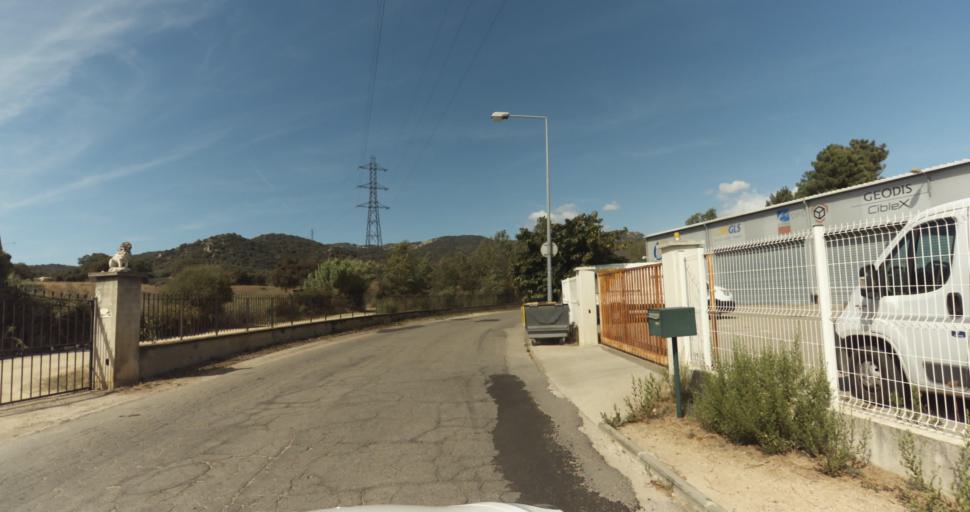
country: FR
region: Corsica
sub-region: Departement de la Corse-du-Sud
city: Ajaccio
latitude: 41.9483
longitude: 8.7630
